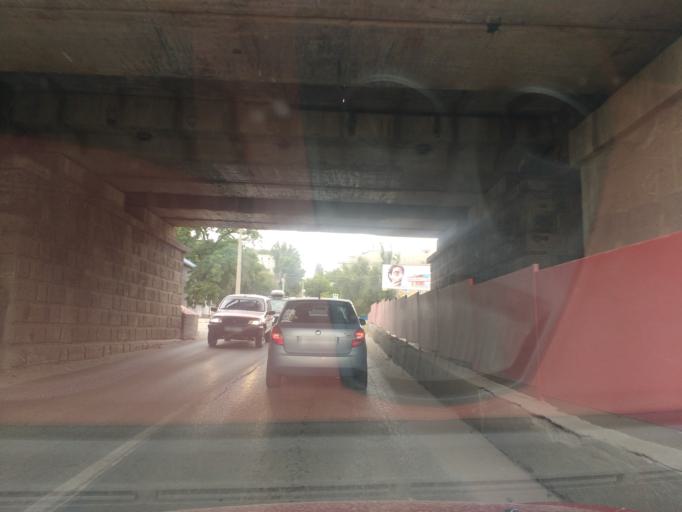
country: RU
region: Volgograd
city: Volgograd
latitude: 48.6950
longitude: 44.4850
